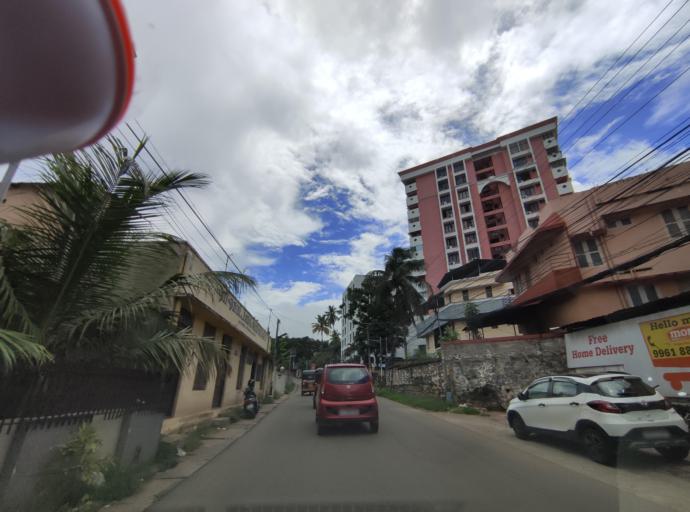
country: IN
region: Kerala
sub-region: Thiruvananthapuram
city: Thiruvananthapuram
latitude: 8.4949
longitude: 76.9634
